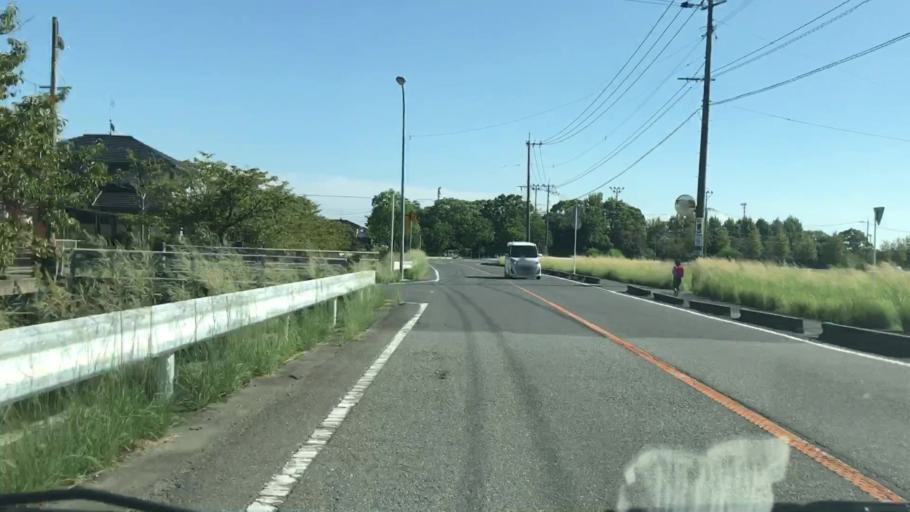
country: JP
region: Saga Prefecture
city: Okawa
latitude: 33.2290
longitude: 130.3558
